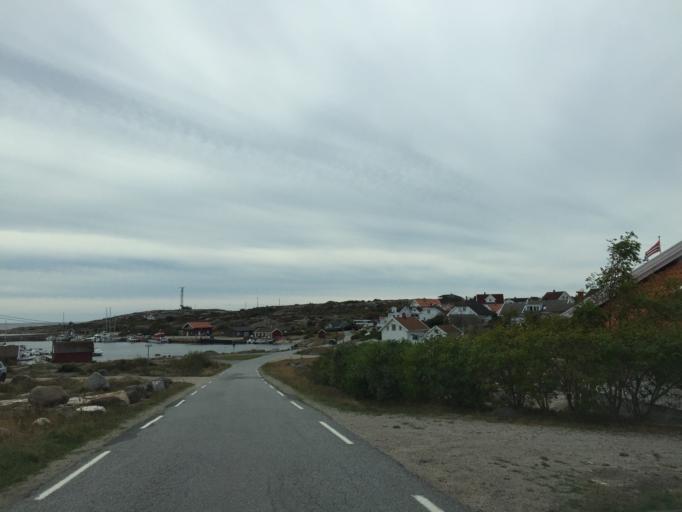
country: NO
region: Ostfold
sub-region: Hvaler
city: Skjaerhalden
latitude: 59.0393
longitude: 10.9497
